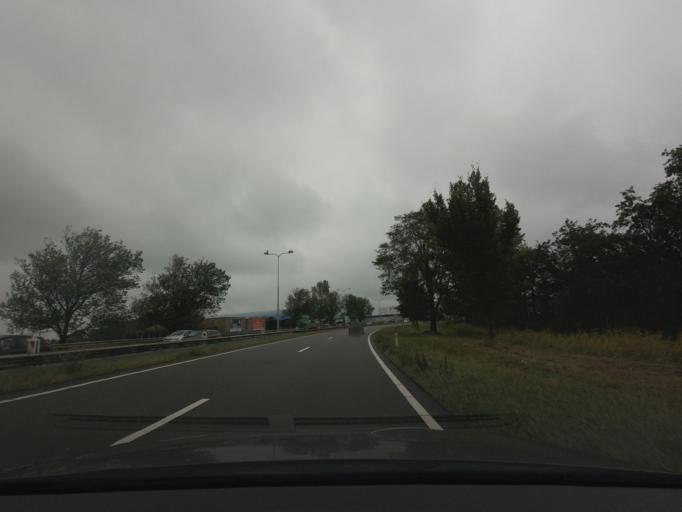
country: NL
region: North Holland
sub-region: Gemeente Alkmaar
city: Alkmaar
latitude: 52.6303
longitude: 4.7121
